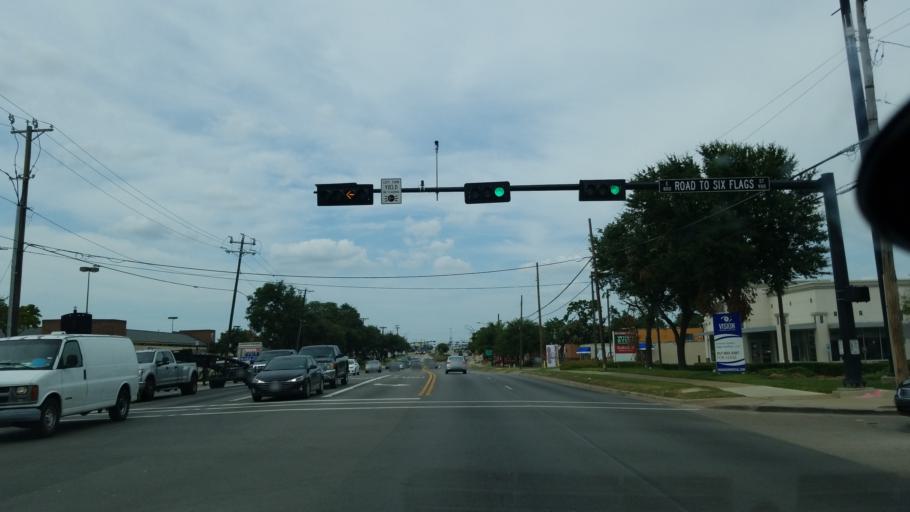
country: US
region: Texas
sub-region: Tarrant County
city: Arlington
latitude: 32.7555
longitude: -97.0972
